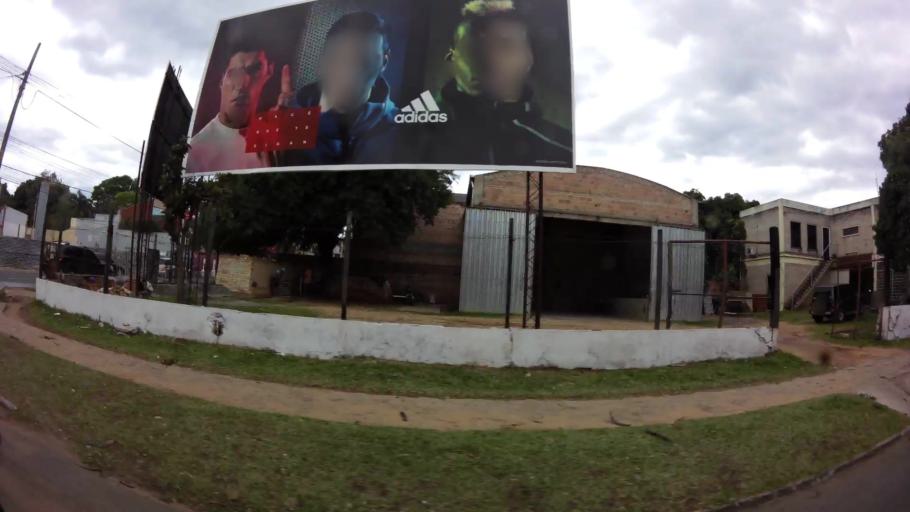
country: PY
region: Central
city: San Lorenzo
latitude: -25.2666
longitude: -57.4963
